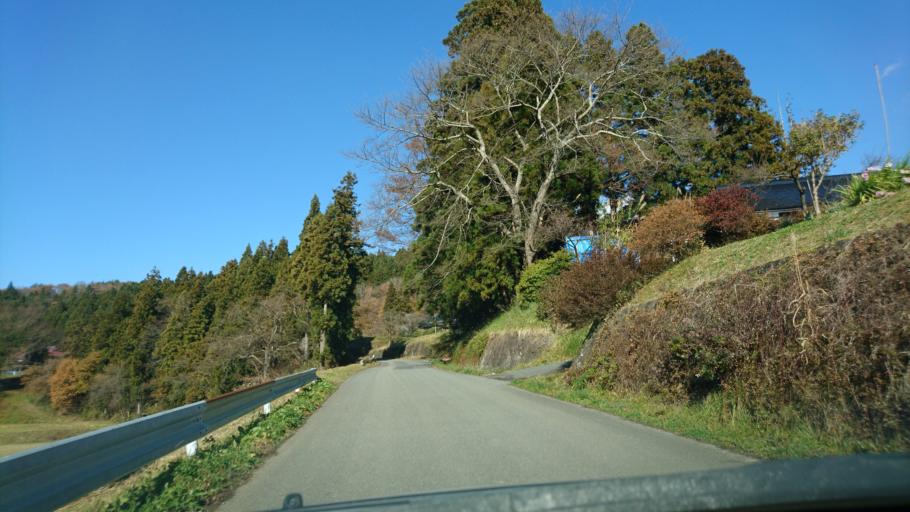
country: JP
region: Iwate
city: Ichinoseki
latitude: 39.0003
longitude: 141.0853
